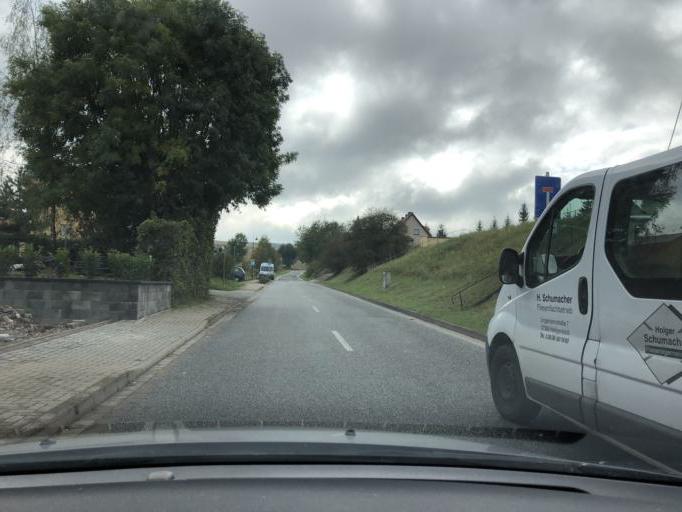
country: DE
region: Thuringia
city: Heuthen
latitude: 51.3298
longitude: 10.2223
